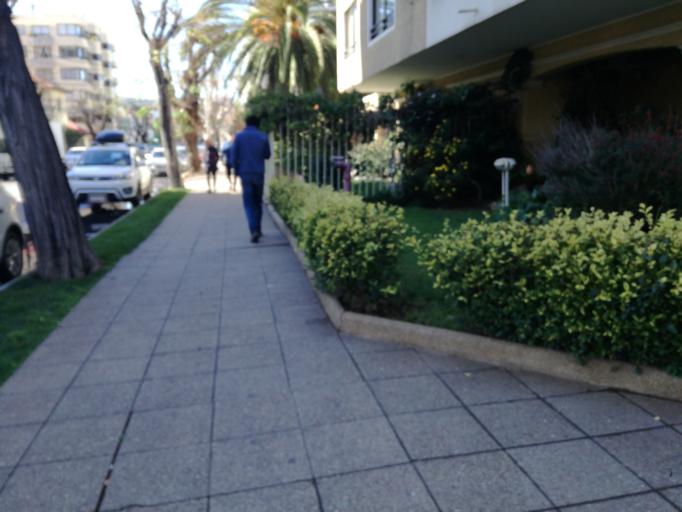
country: CL
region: Valparaiso
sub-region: Provincia de Valparaiso
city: Vina del Mar
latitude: -33.0202
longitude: -71.5535
